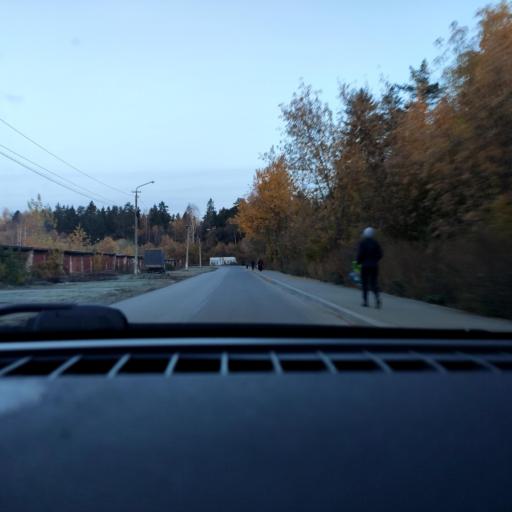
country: RU
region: Perm
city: Kondratovo
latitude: 57.9761
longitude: 56.1547
